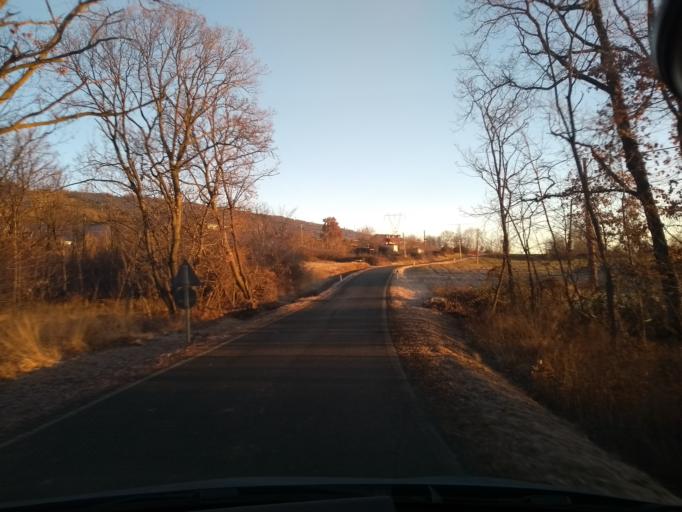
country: IT
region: Piedmont
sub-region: Provincia di Torino
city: Balangero
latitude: 45.2777
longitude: 7.5390
